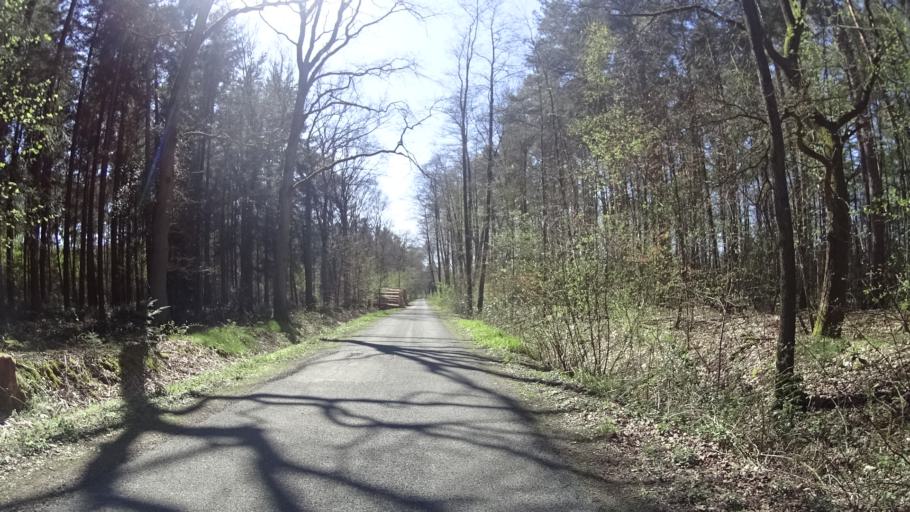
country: DE
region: North Rhine-Westphalia
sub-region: Regierungsbezirk Munster
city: Dulmen
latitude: 51.7845
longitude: 7.2531
